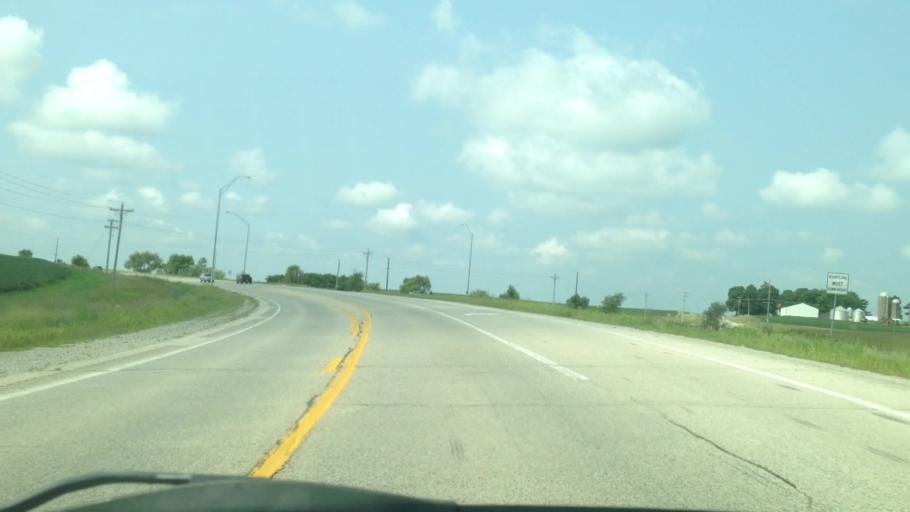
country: US
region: Iowa
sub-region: Benton County
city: Walford
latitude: 41.8761
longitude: -91.8658
